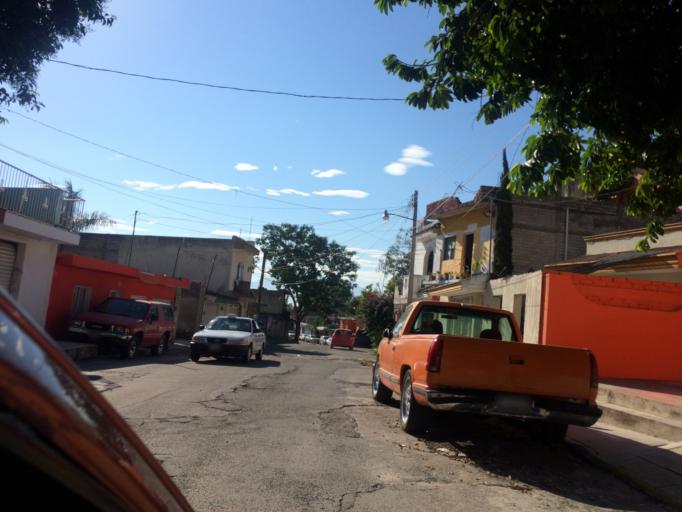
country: MX
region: Nayarit
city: Tepic
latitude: 21.4997
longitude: -104.9140
